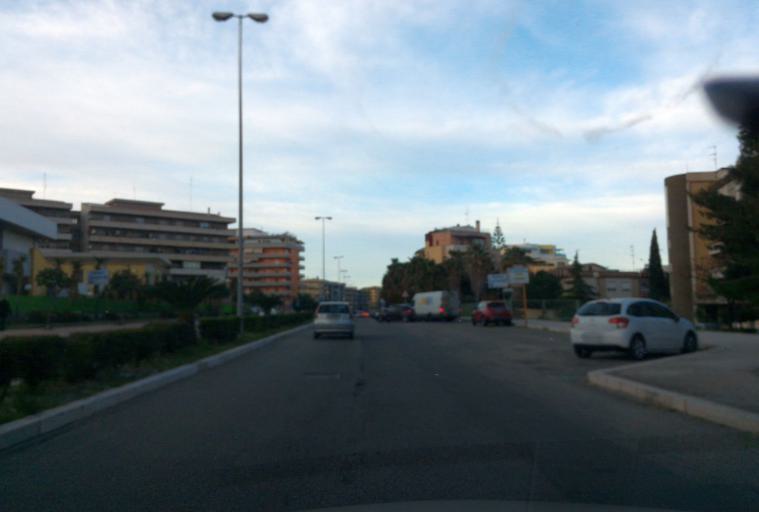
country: IT
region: Calabria
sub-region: Provincia di Crotone
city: Crotone
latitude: 39.0699
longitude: 17.1285
